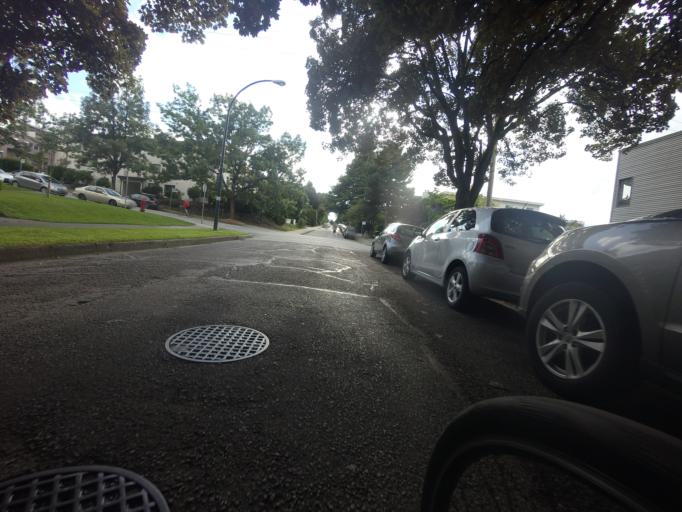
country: CA
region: British Columbia
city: West End
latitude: 49.2689
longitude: -123.1500
